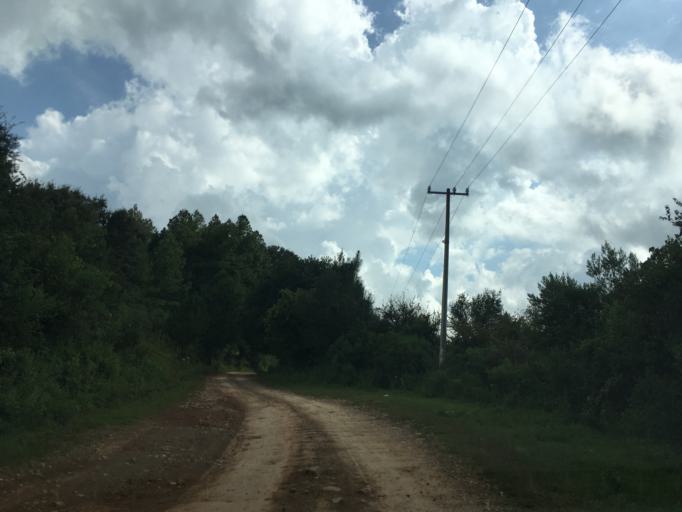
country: MX
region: Michoacan
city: Acuitzio del Canje
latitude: 19.5172
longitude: -101.2111
